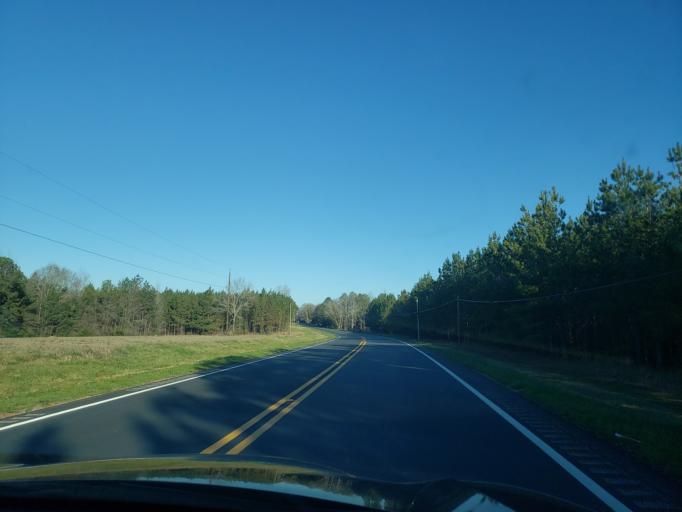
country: US
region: Alabama
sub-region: Macon County
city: Tuskegee
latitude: 32.5734
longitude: -85.6898
